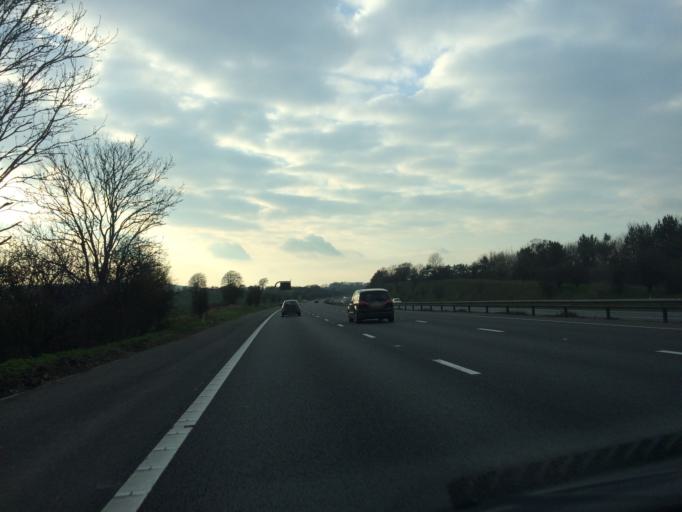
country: GB
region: England
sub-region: Borough of Swindon
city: Bishopstone
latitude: 51.5164
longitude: -1.6519
